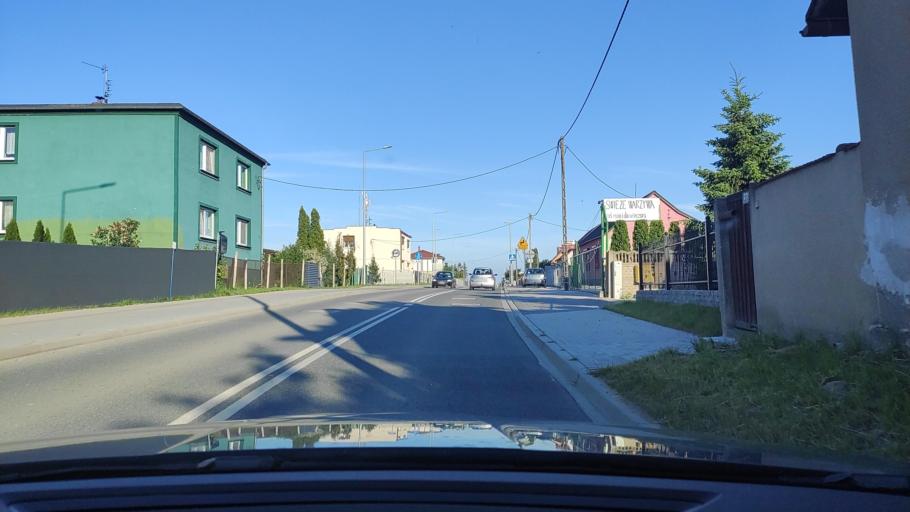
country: PL
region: Greater Poland Voivodeship
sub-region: Powiat poznanski
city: Kornik
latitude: 52.3056
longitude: 17.0799
